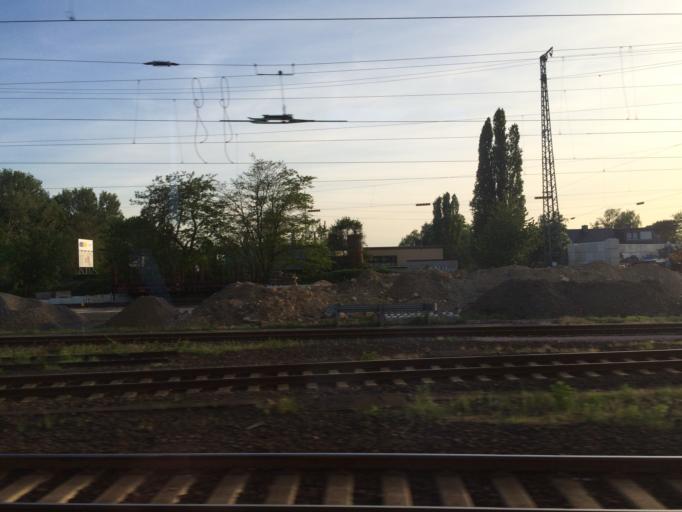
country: DE
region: Hesse
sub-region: Regierungsbezirk Darmstadt
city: Hanau am Main
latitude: 50.1169
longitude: 8.9352
